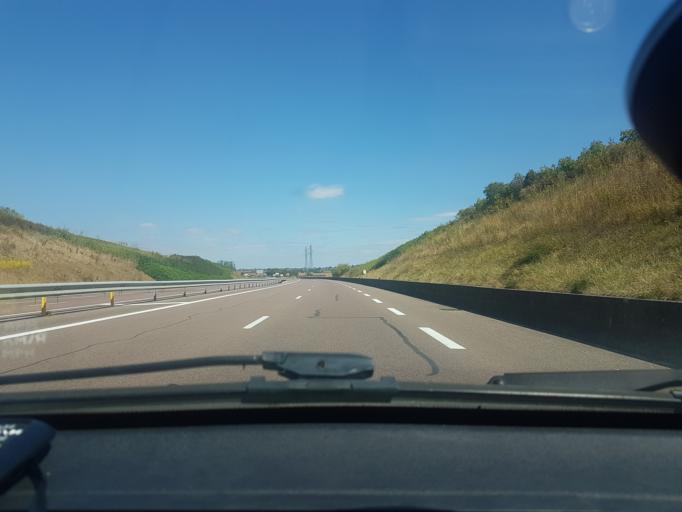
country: FR
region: Bourgogne
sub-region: Departement de la Cote-d'Or
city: Quetigny
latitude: 47.3261
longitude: 5.1022
